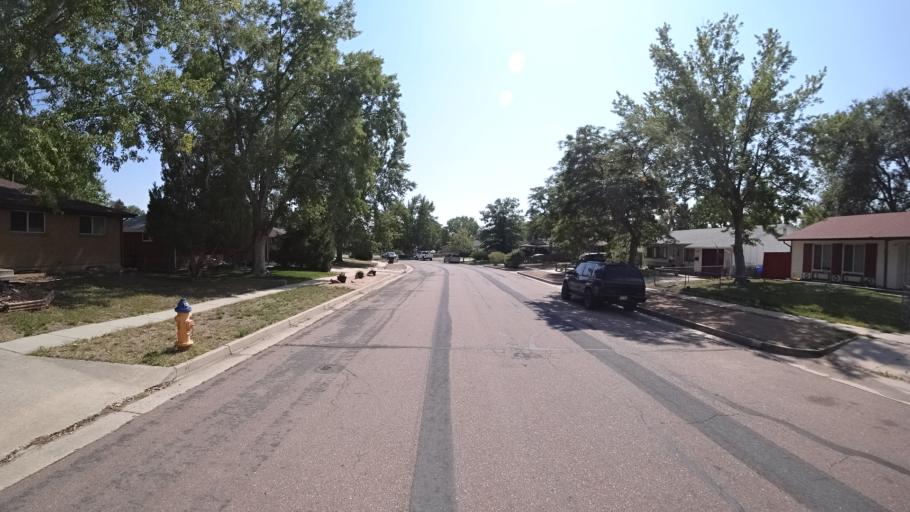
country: US
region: Colorado
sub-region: El Paso County
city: Colorado Springs
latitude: 38.8288
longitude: -104.7696
